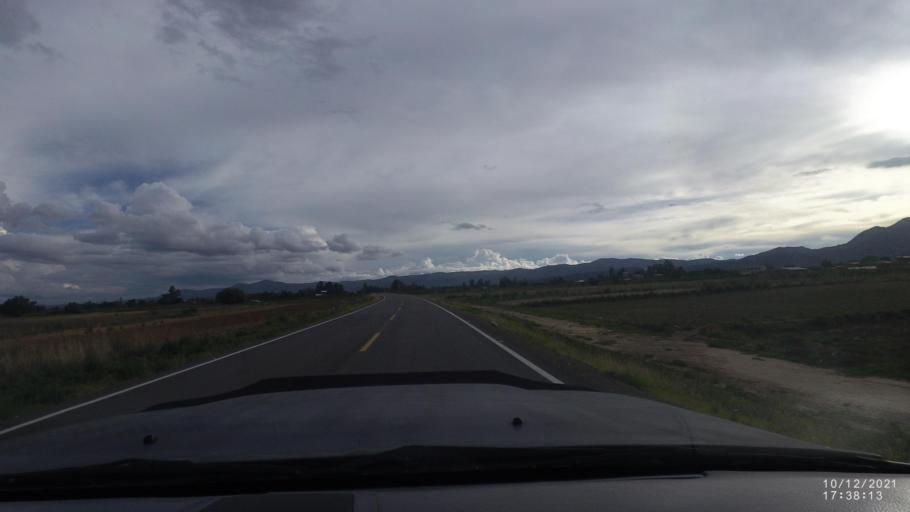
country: BO
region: Cochabamba
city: Tarata
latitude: -17.5670
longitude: -66.0091
